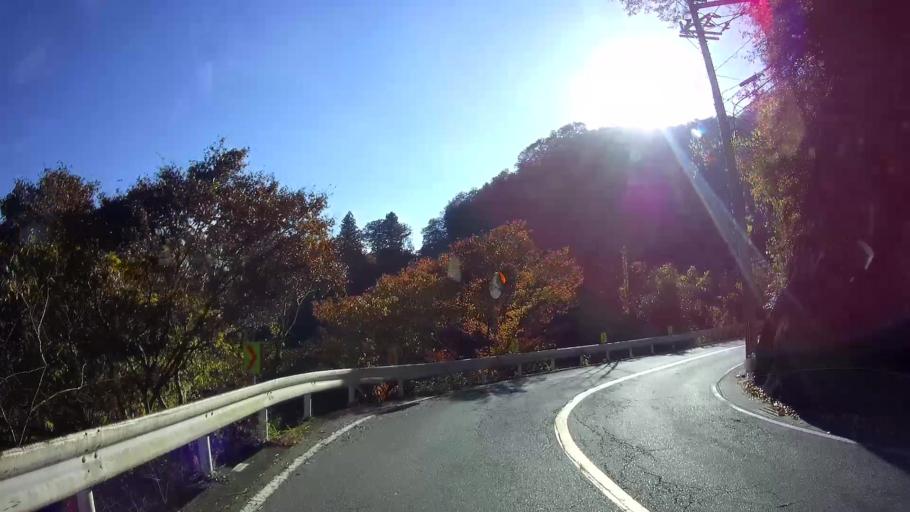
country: JP
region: Yamanashi
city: Uenohara
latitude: 35.6045
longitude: 139.1241
